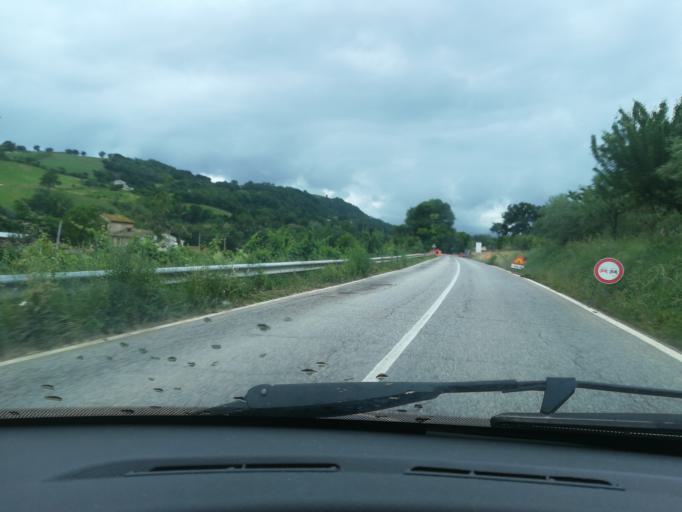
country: IT
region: The Marches
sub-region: Provincia di Macerata
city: San Ginesio
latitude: 43.1021
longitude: 13.3484
